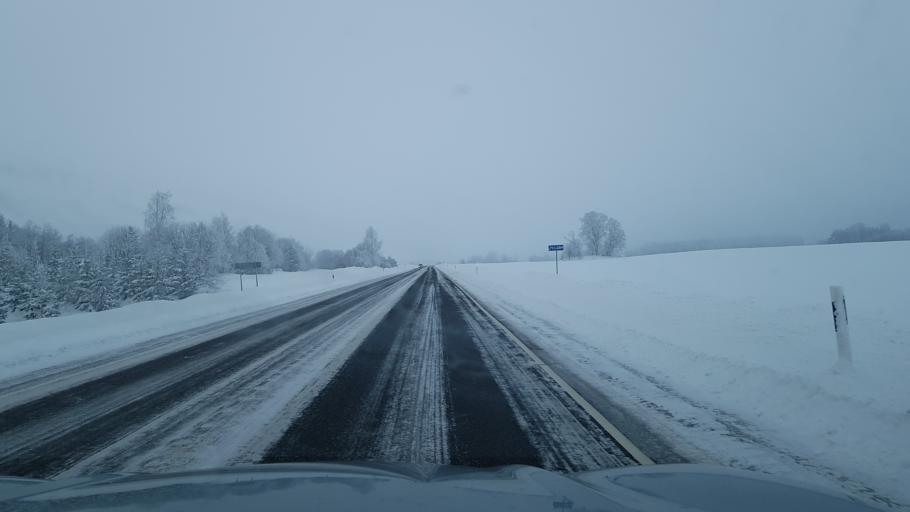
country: EE
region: Ida-Virumaa
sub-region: Johvi vald
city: Johvi
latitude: 59.2456
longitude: 27.3668
